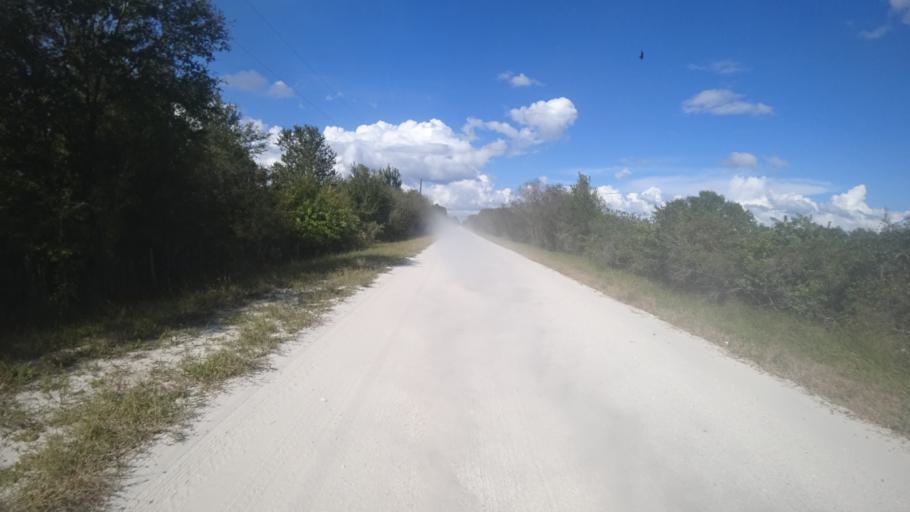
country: US
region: Florida
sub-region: DeSoto County
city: Arcadia
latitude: 27.3155
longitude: -82.0805
